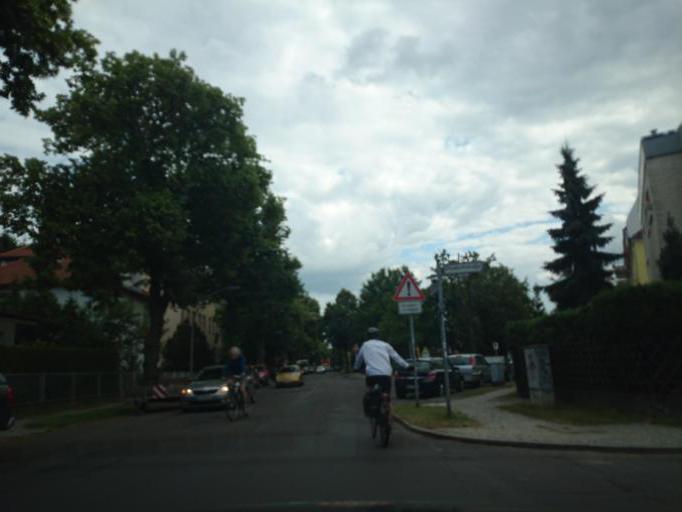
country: DE
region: Berlin
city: Lichtenrade
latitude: 52.3899
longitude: 13.3936
